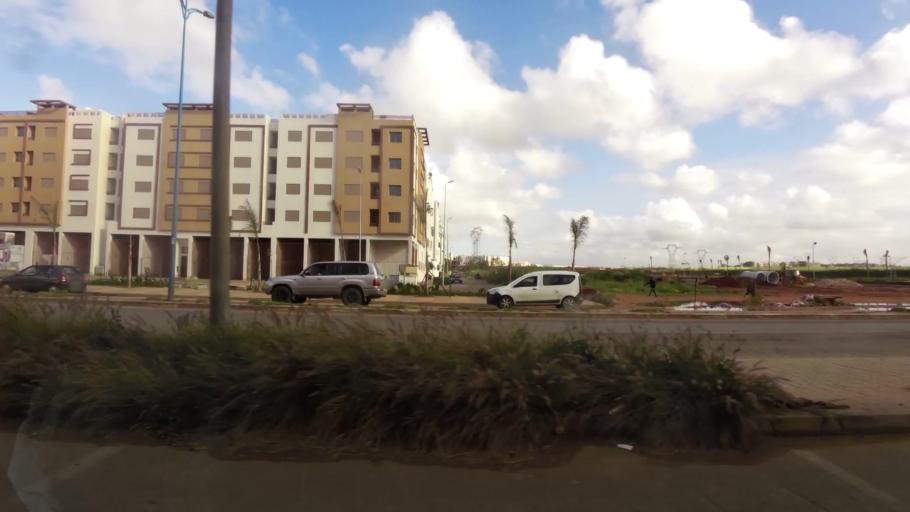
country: MA
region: Grand Casablanca
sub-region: Casablanca
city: Casablanca
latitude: 33.5478
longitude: -7.7026
